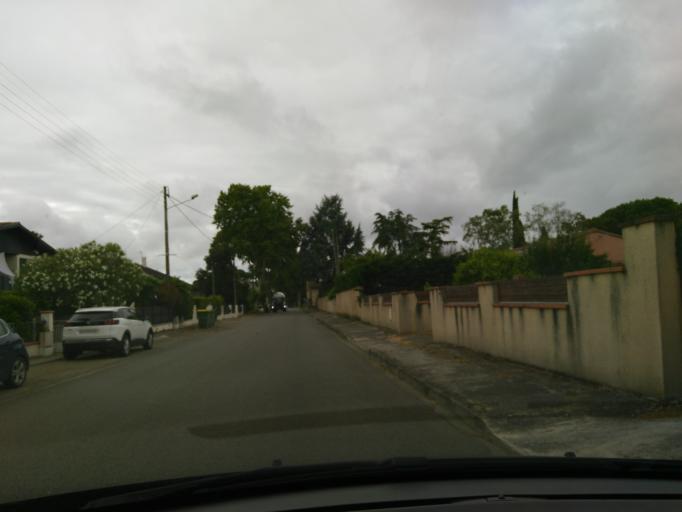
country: FR
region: Midi-Pyrenees
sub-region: Departement de la Haute-Garonne
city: Grenade
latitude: 43.7761
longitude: 1.2896
